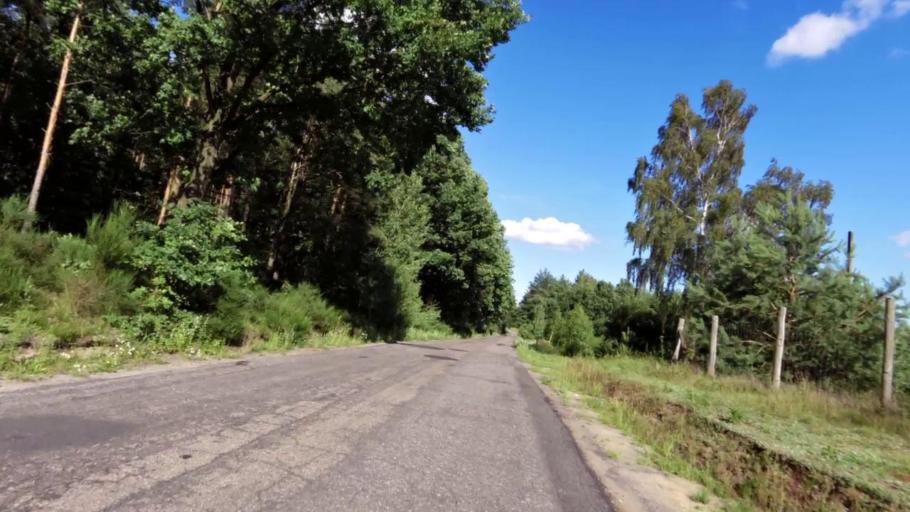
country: PL
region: West Pomeranian Voivodeship
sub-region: Powiat slawienski
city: Slawno
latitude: 54.4365
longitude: 16.7584
